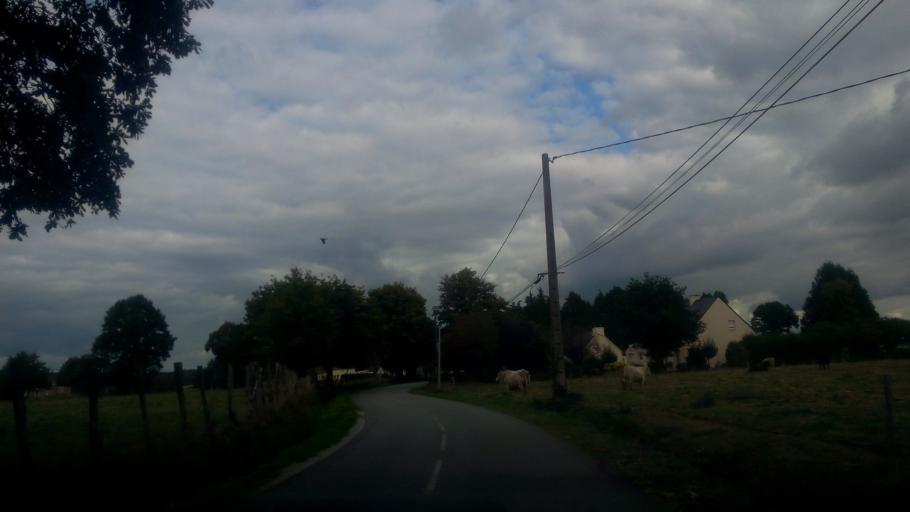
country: FR
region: Brittany
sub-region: Departement du Morbihan
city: Saint-Jean-la-Poterie
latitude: 47.6558
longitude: -2.1235
